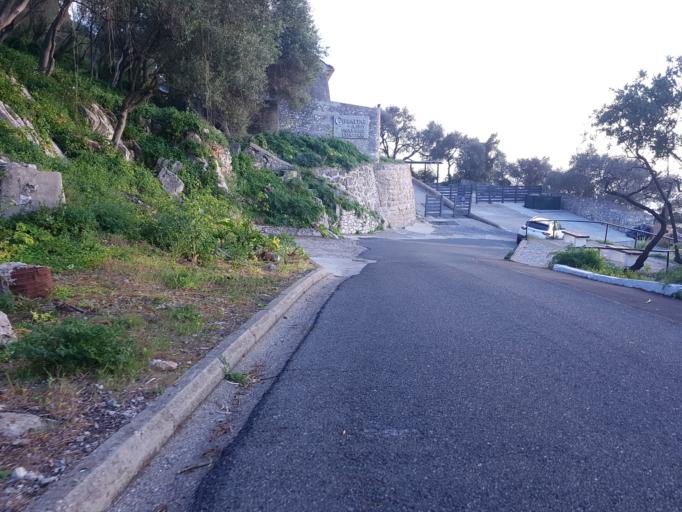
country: GI
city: Gibraltar
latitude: 36.1432
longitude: -5.3484
